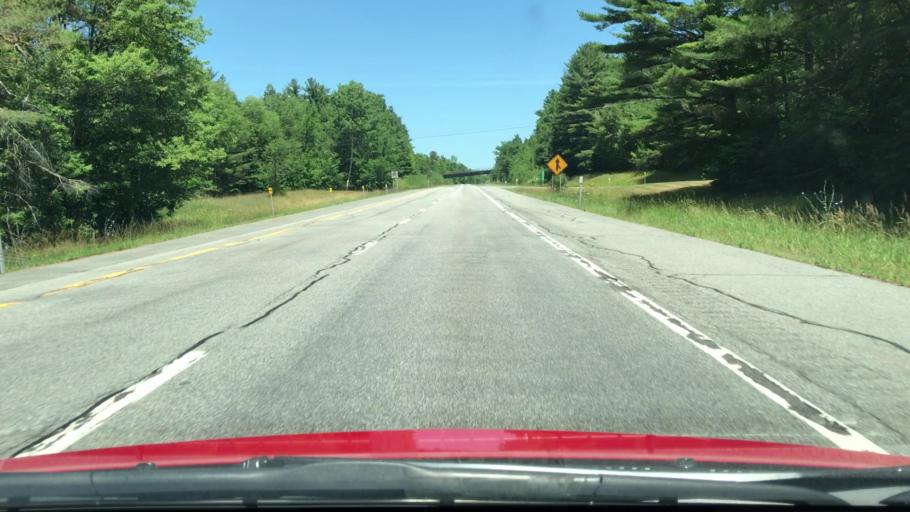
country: US
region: New York
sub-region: Essex County
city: Elizabethtown
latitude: 44.1634
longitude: -73.5835
